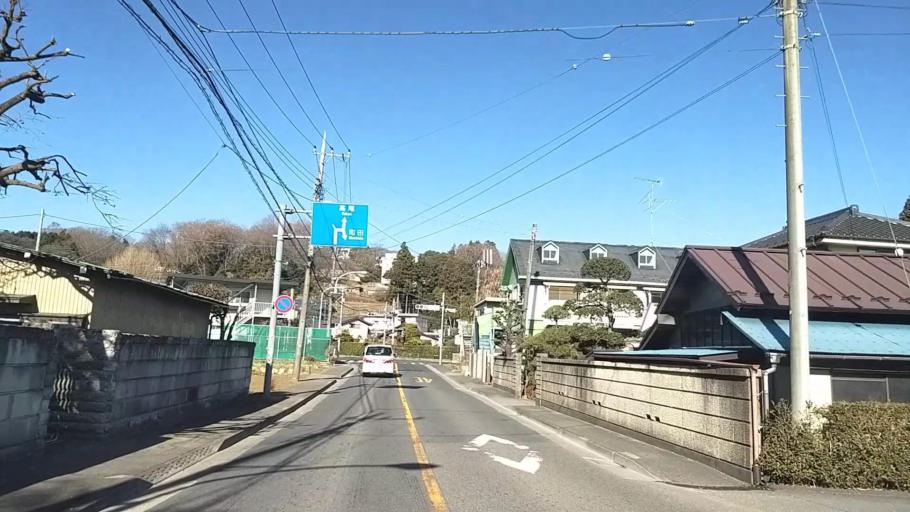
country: JP
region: Tokyo
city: Hachioji
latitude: 35.6125
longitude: 139.2900
